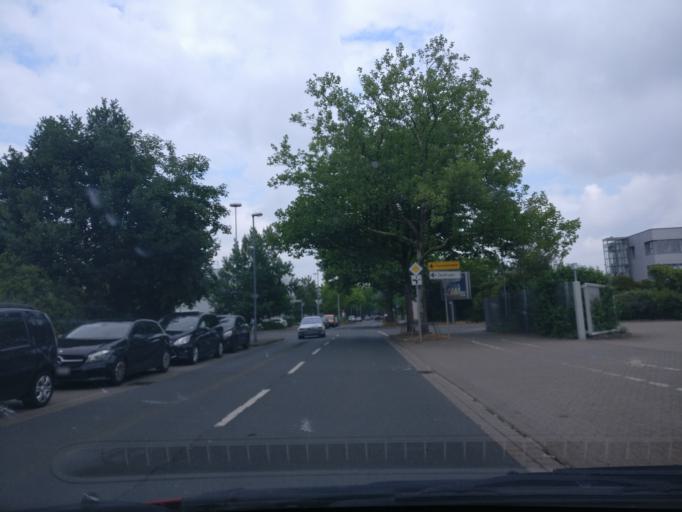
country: DE
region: Lower Saxony
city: Laatzen
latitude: 52.3353
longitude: 9.7746
